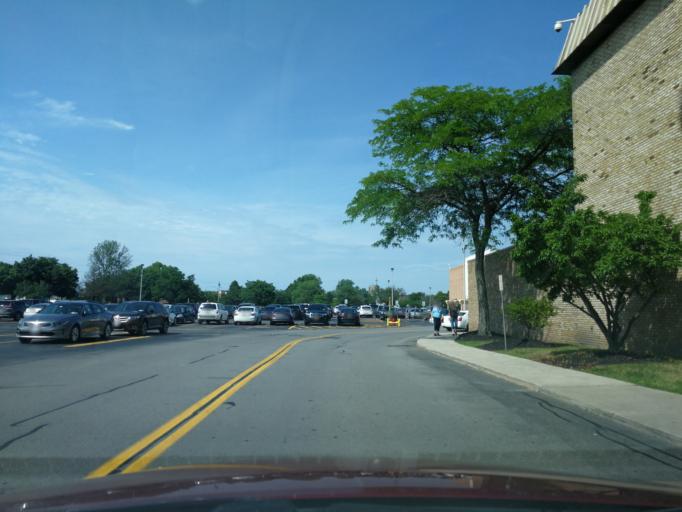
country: US
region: New York
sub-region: Monroe County
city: Greece
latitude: 43.2062
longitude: -77.6945
